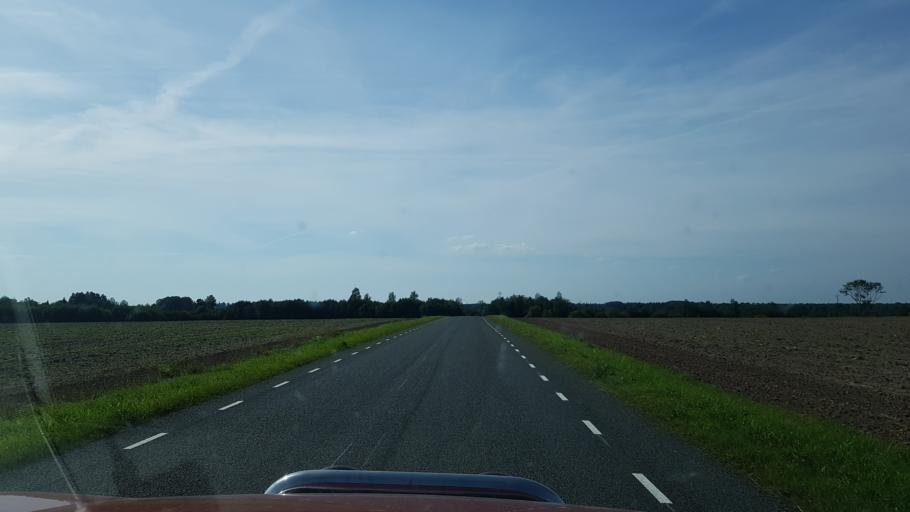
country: EE
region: Viljandimaa
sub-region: Abja vald
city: Abja-Paluoja
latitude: 58.3378
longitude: 25.2579
